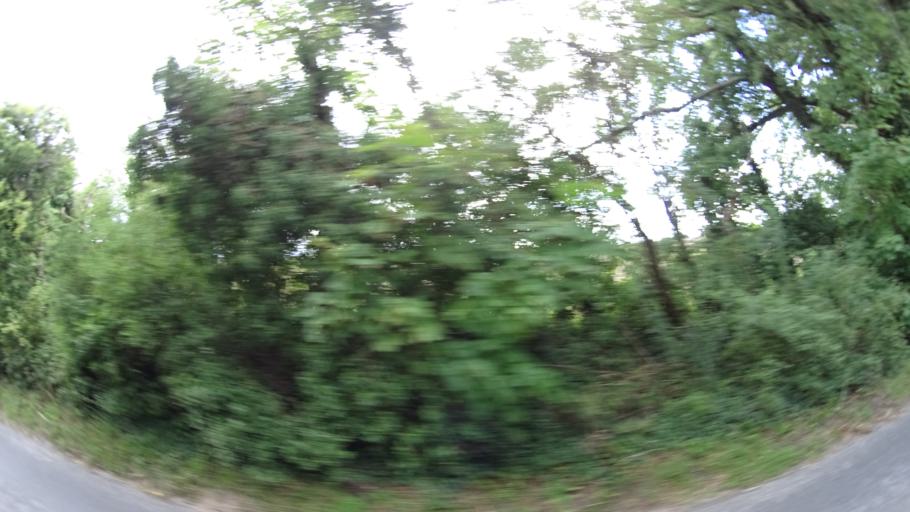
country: GB
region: England
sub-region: Hampshire
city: East Dean
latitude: 51.0860
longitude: -1.5639
